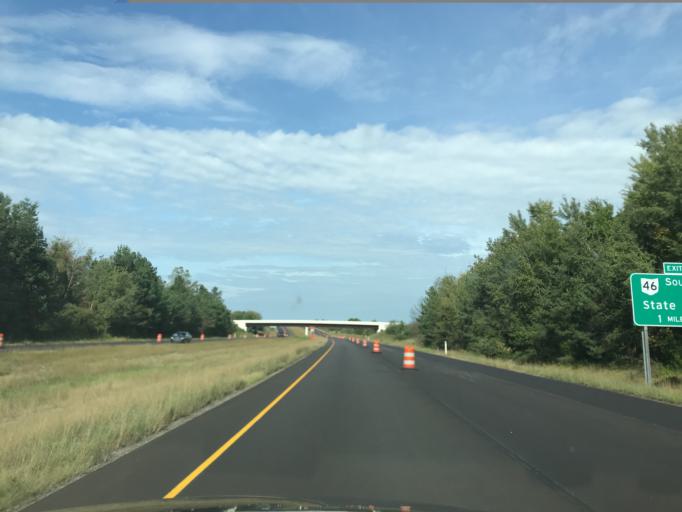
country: US
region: Ohio
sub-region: Ashtabula County
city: Jefferson
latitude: 41.7944
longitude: -80.7417
